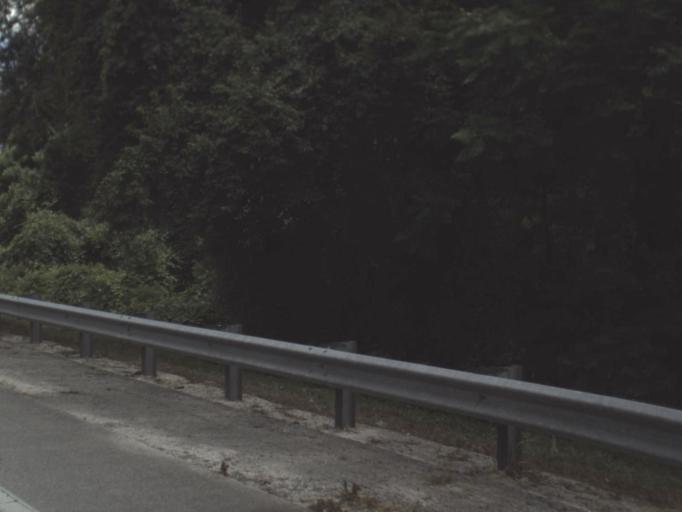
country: US
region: Florida
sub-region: Putnam County
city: Palatka
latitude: 29.5416
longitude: -81.6485
